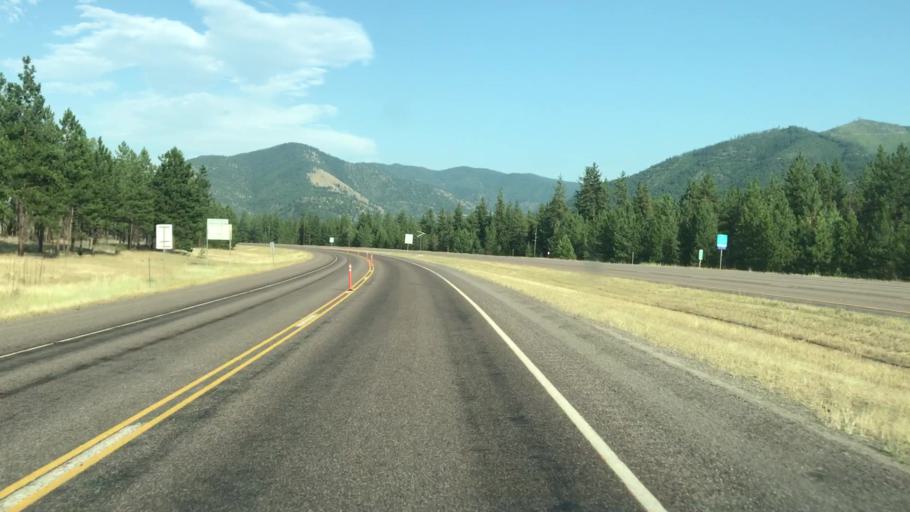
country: US
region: Montana
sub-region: Mineral County
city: Superior
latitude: 47.0127
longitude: -114.7260
